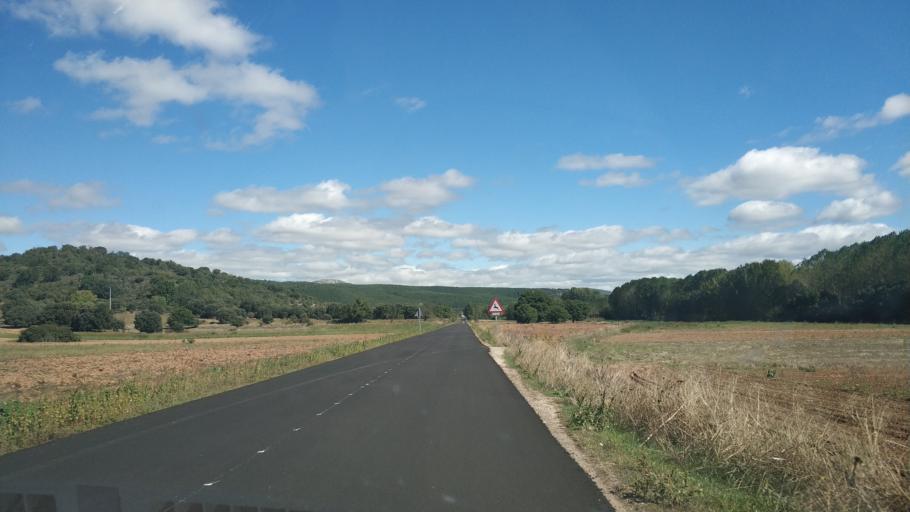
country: ES
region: Castille and Leon
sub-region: Provincia de Burgos
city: Puentedura
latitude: 42.0453
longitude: -3.5787
